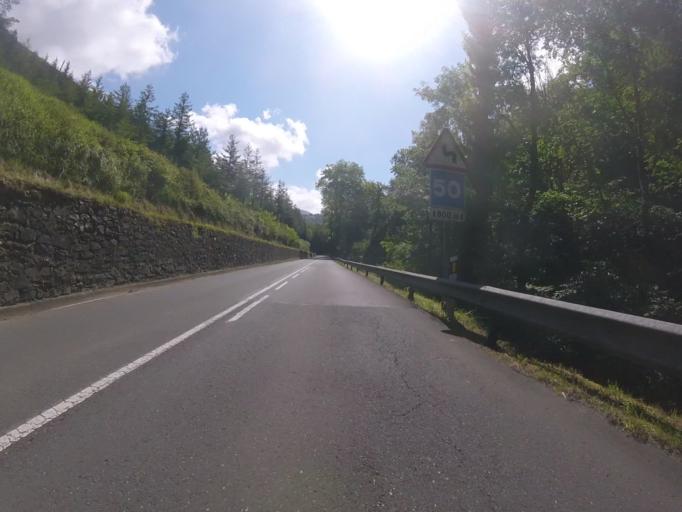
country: ES
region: Basque Country
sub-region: Provincia de Guipuzcoa
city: Azpeitia
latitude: 43.1785
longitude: -2.2395
